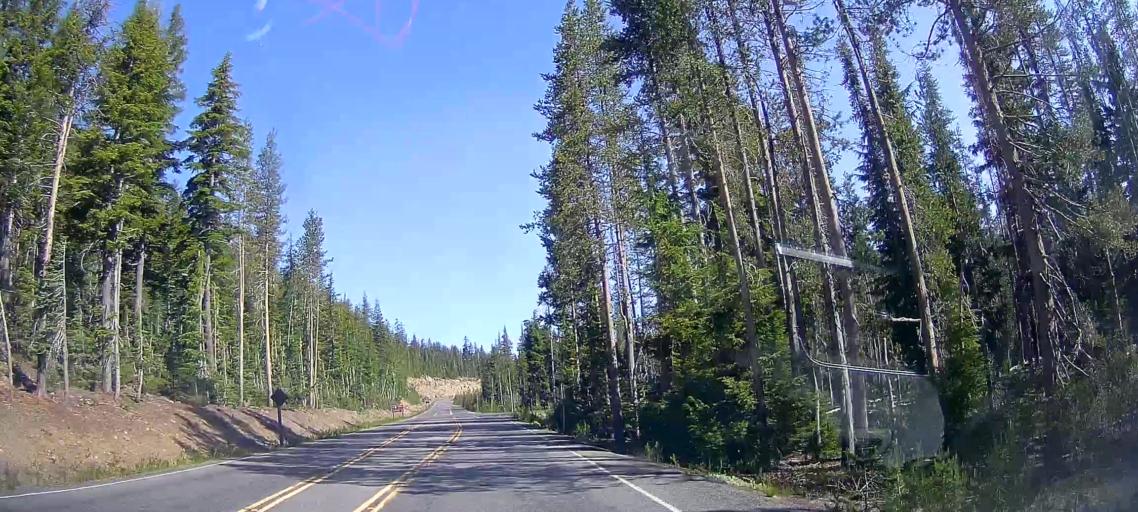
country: US
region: Oregon
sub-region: Jackson County
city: Shady Cove
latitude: 42.8646
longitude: -122.1683
